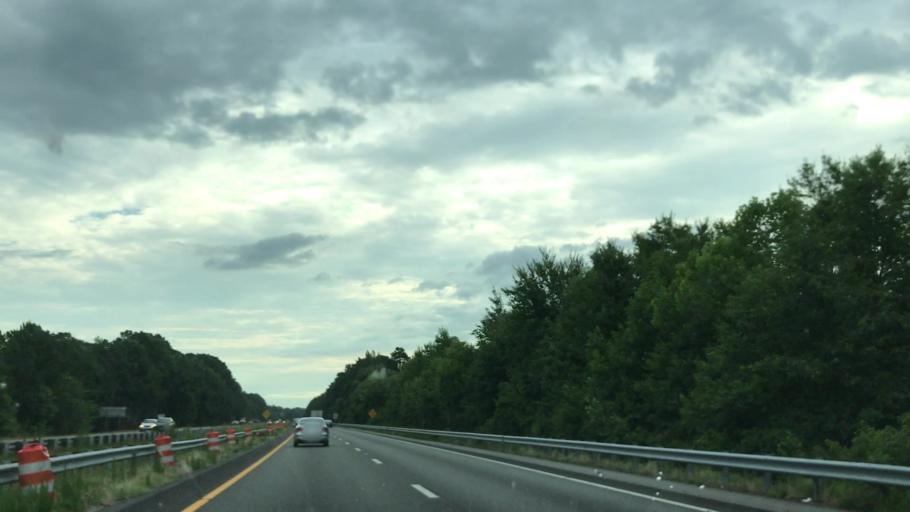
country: US
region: North Carolina
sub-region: Johnston County
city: Four Oaks
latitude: 35.4619
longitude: -78.3847
